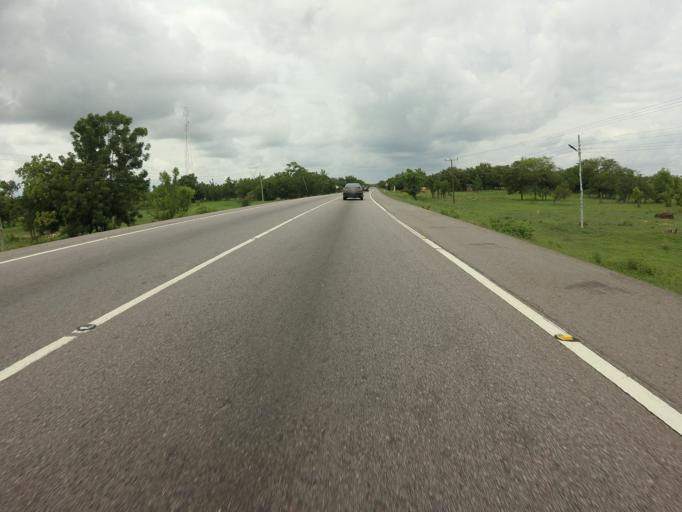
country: GH
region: Northern
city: Tamale
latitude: 8.8895
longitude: -1.4213
